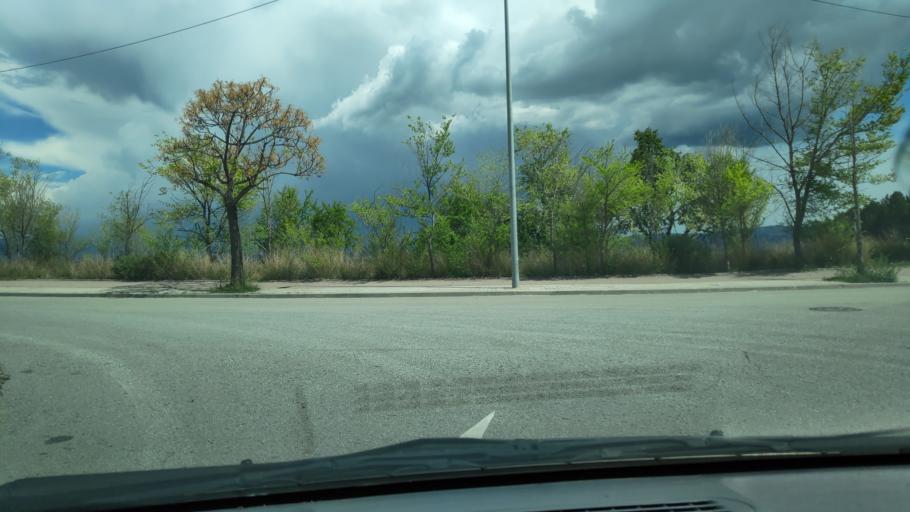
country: ES
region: Catalonia
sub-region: Provincia de Barcelona
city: Polinya
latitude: 41.5378
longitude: 2.1394
